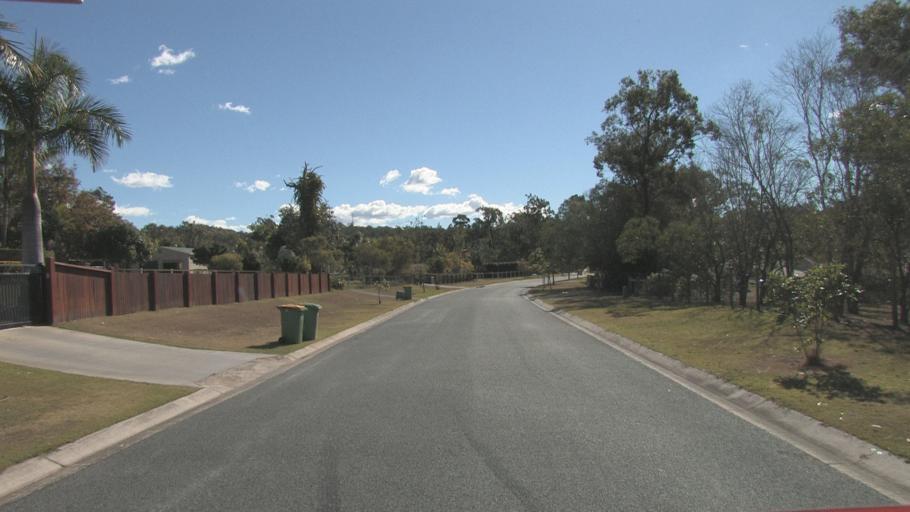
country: AU
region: Queensland
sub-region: Ipswich
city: Springfield Lakes
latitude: -27.7262
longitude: 152.9177
